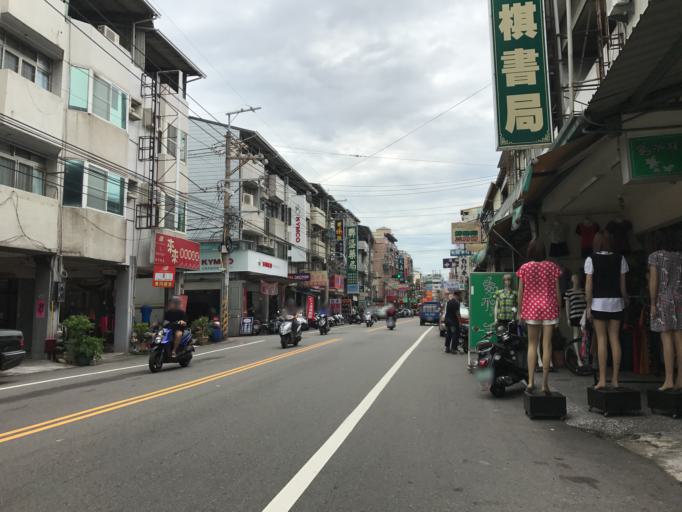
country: TW
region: Taiwan
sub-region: Taichung City
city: Taichung
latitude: 24.0873
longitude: 120.7068
